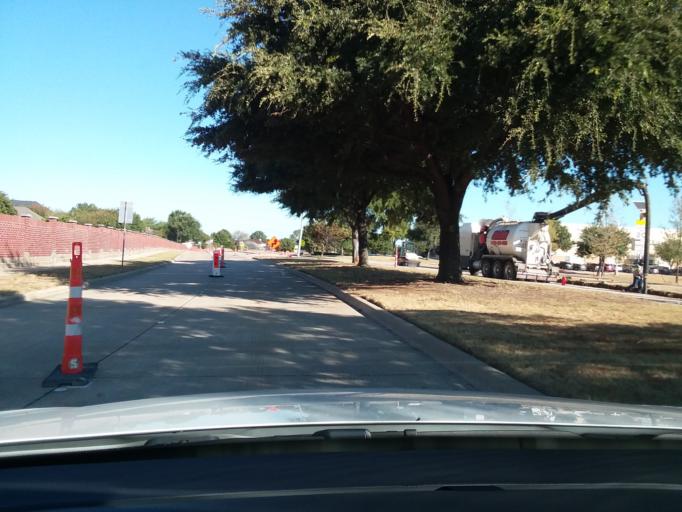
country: US
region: Texas
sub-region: Denton County
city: Lewisville
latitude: 33.0593
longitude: -97.0191
